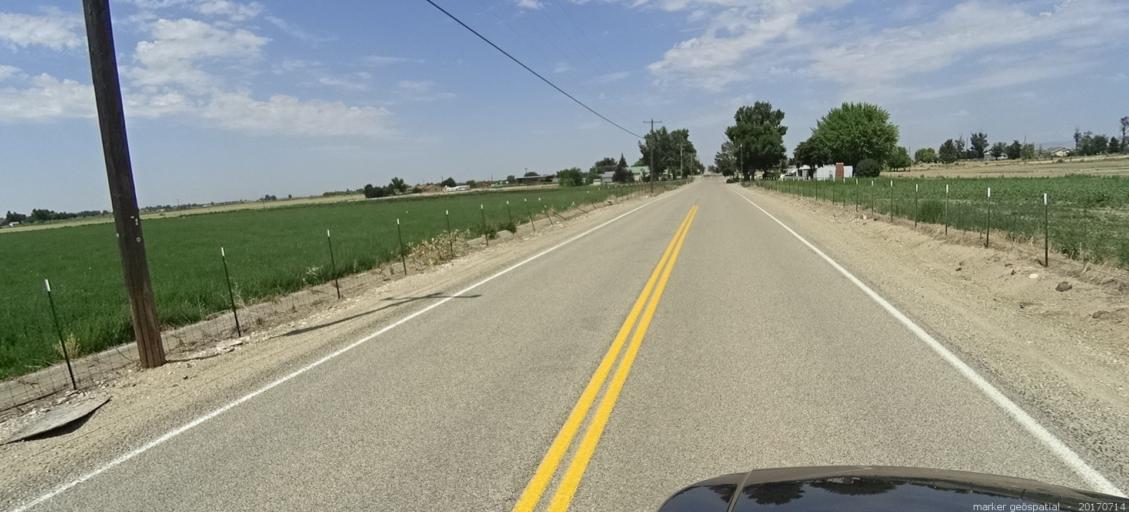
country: US
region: Idaho
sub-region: Ada County
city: Kuna
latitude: 43.5291
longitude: -116.3543
